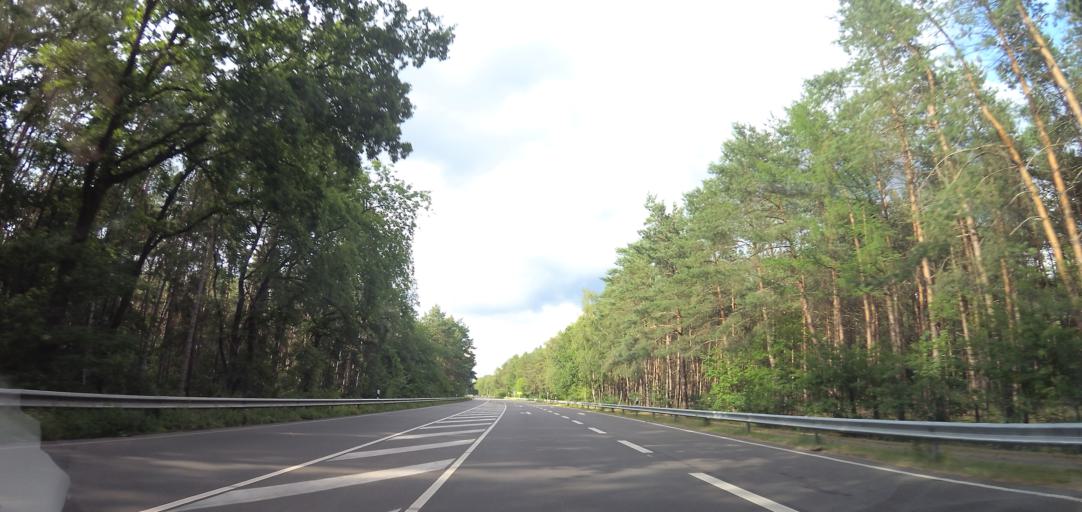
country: DE
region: Lower Saxony
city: Niederlangen
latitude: 52.8147
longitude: 7.3211
